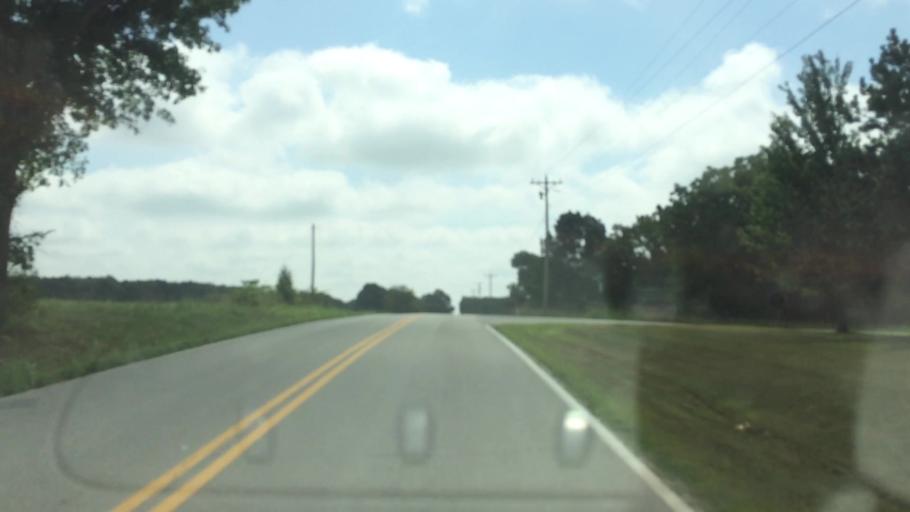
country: US
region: Missouri
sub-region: Greene County
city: Strafford
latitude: 37.2723
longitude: -93.2094
